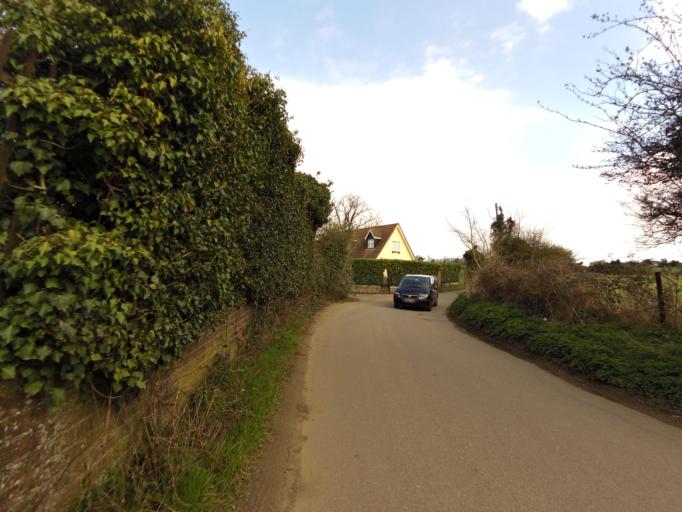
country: GB
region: England
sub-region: Suffolk
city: Ipswich
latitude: 52.0917
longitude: 1.1399
